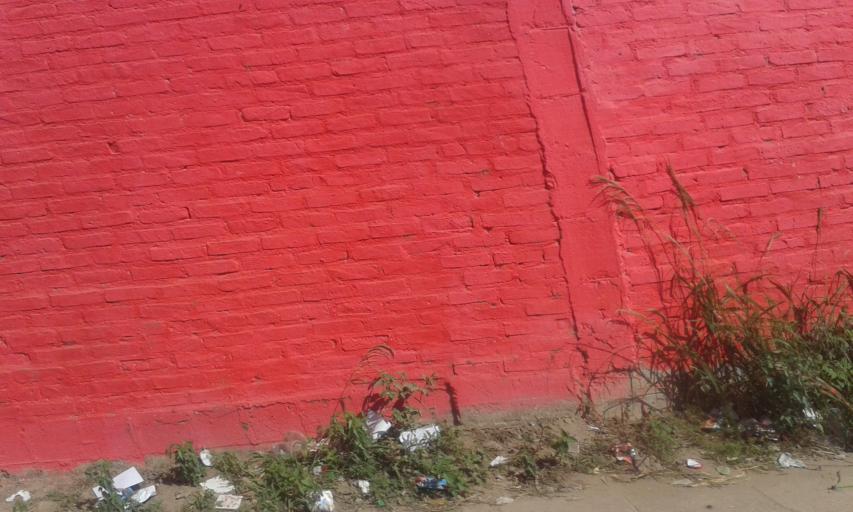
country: BO
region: Santa Cruz
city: Santa Cruz de la Sierra
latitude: -17.7722
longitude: -63.2046
